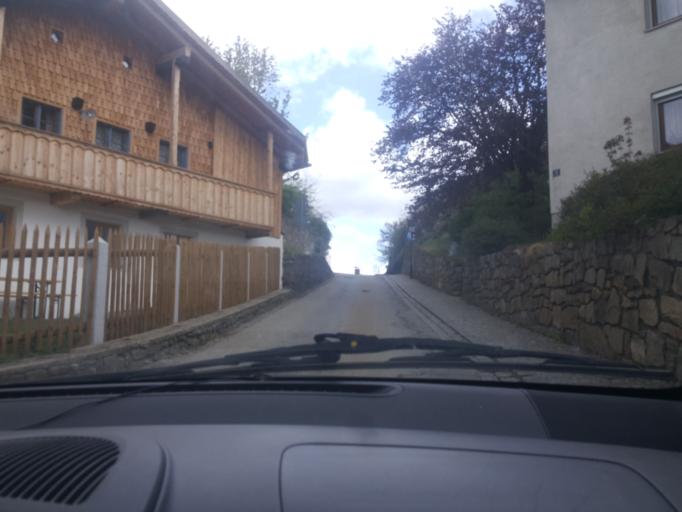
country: DE
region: Bavaria
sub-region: Lower Bavaria
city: Kollnburg
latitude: 49.0463
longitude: 12.8614
